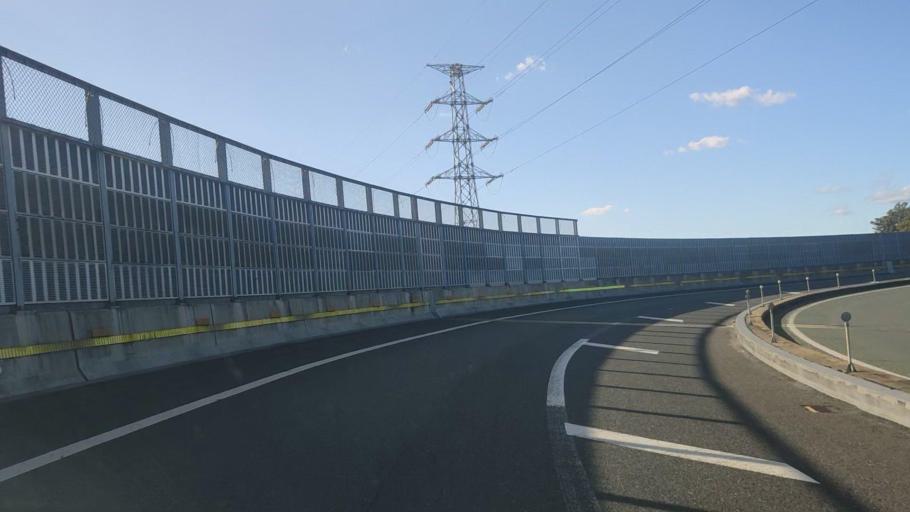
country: JP
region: Fukuoka
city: Nogata
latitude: 33.7790
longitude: 130.7417
